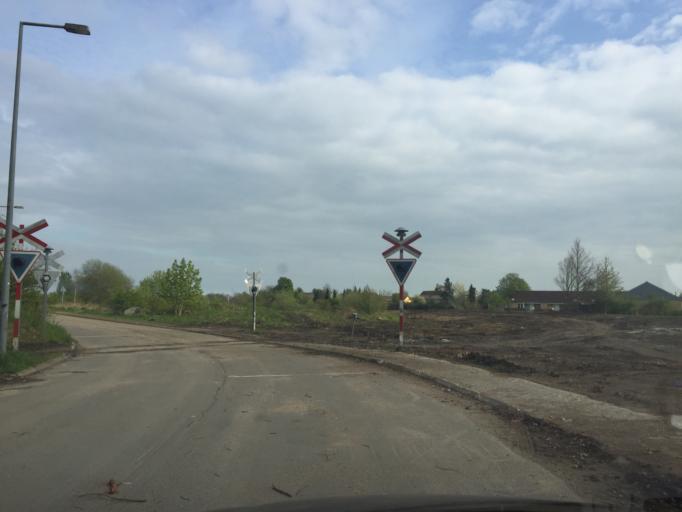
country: DK
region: Capital Region
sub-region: Hoje-Taastrup Kommune
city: Flong
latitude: 55.6469
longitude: 12.1958
